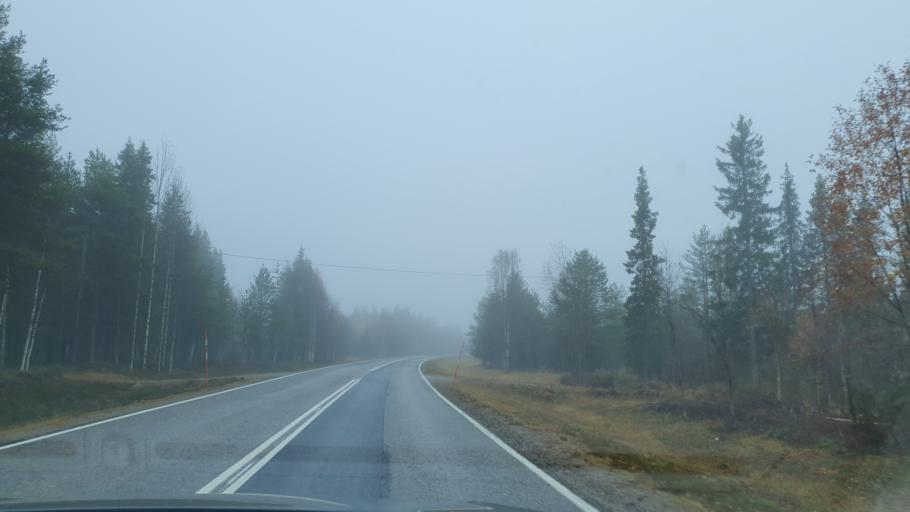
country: FI
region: Lapland
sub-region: Tunturi-Lappi
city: Kittilae
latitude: 67.2912
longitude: 24.8872
